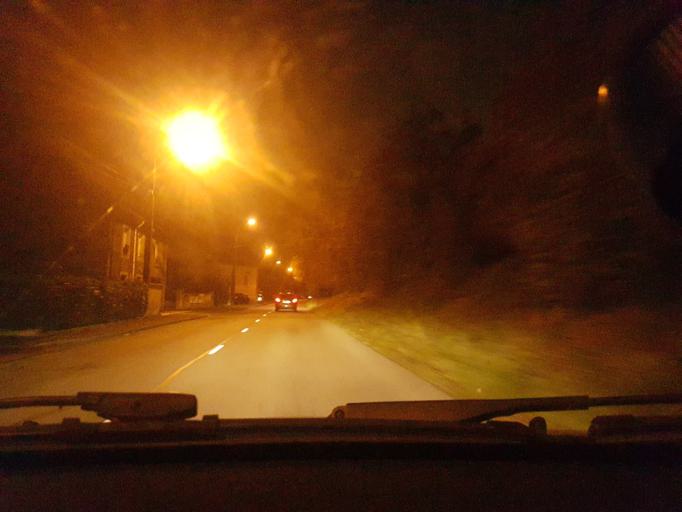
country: FR
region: Franche-Comte
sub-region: Territoire de Belfort
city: Danjoutin
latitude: 47.6209
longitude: 6.8658
